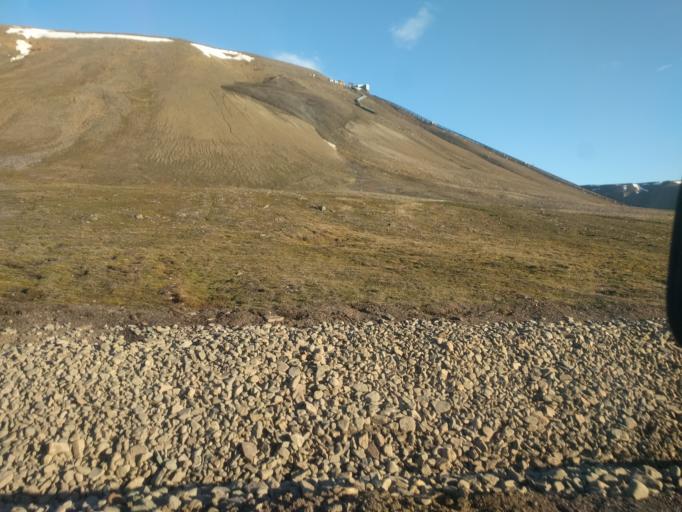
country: SJ
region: Svalbard
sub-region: Spitsbergen
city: Longyearbyen
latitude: 78.1731
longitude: 15.9418
